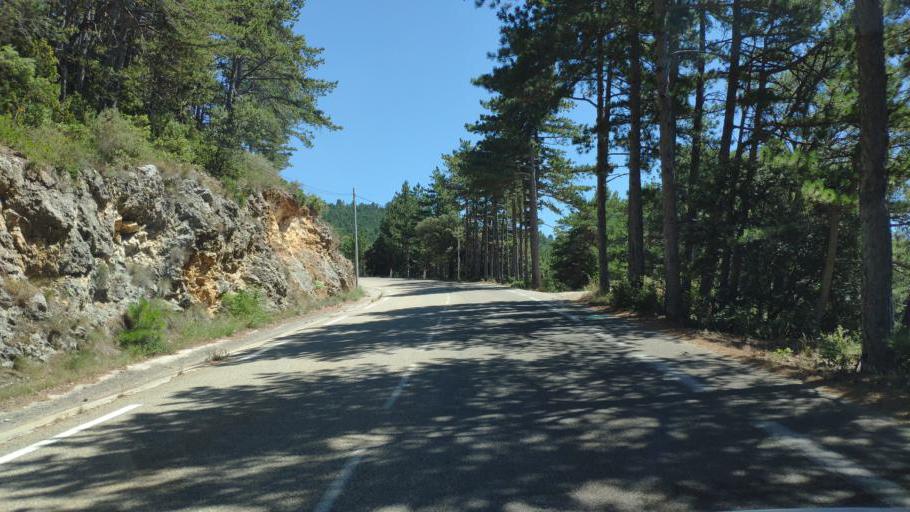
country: FR
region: Provence-Alpes-Cote d'Azur
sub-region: Departement du Vaucluse
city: Malaucene
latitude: 44.1606
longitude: 5.1415
